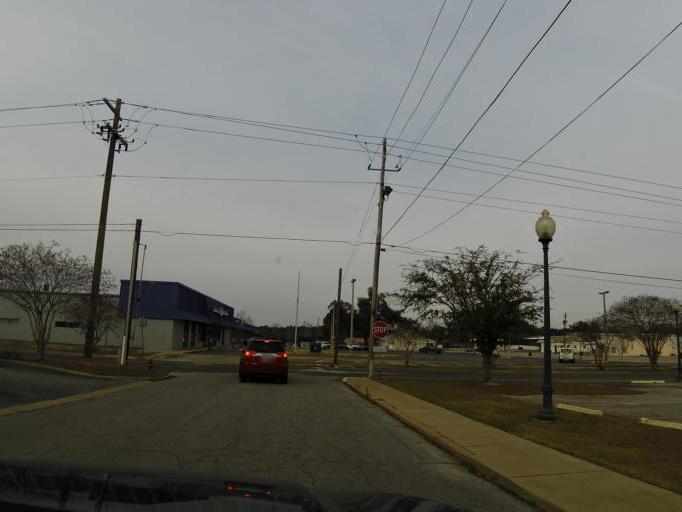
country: US
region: Georgia
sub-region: Decatur County
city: Bainbridge
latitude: 30.9076
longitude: -84.5773
